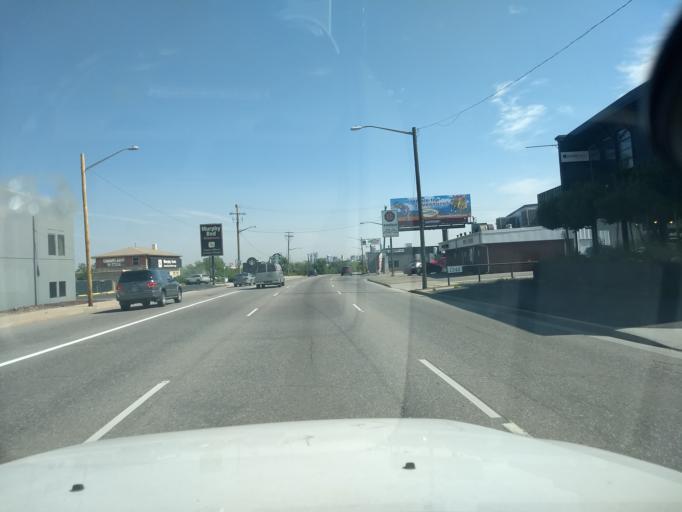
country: US
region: Colorado
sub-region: Arapahoe County
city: Englewood
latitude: 39.6923
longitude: -104.9924
